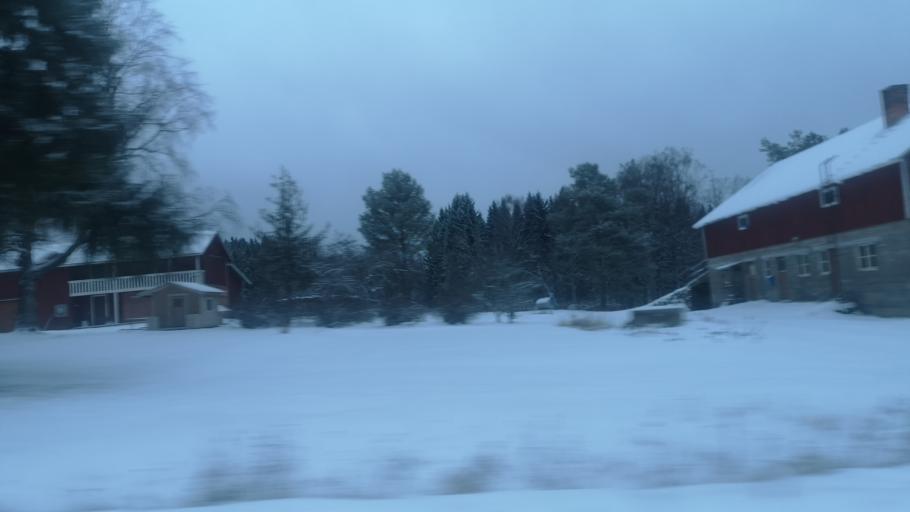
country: FI
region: Southern Savonia
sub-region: Savonlinna
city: Enonkoski
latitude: 62.0622
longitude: 28.7294
